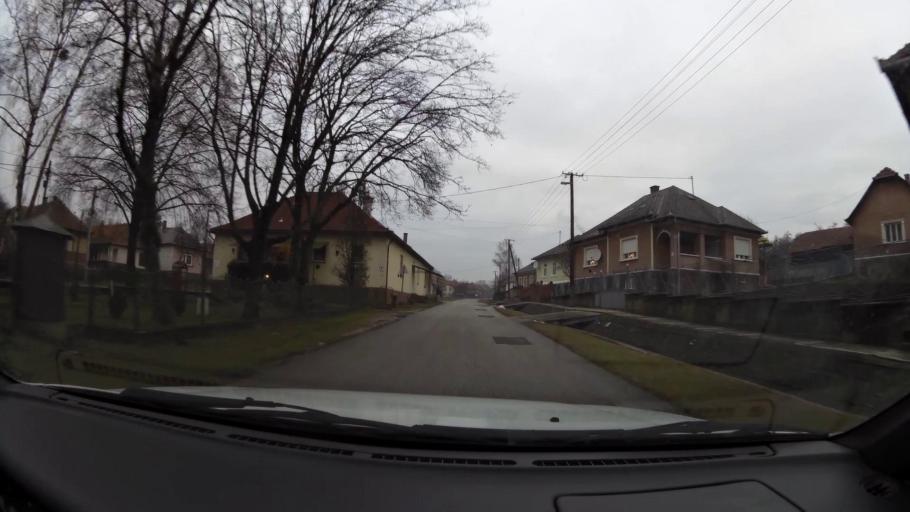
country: HU
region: Borsod-Abauj-Zemplen
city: Rudabanya
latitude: 48.4106
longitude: 20.6546
